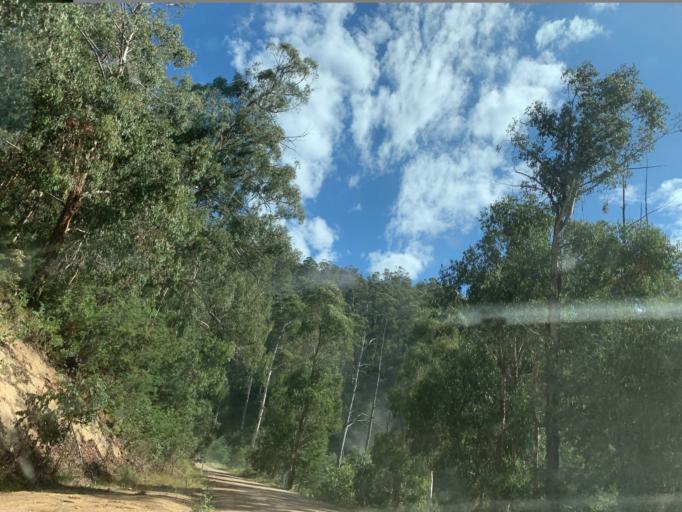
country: AU
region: Victoria
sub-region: Mansfield
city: Mansfield
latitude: -37.0994
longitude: 146.5120
